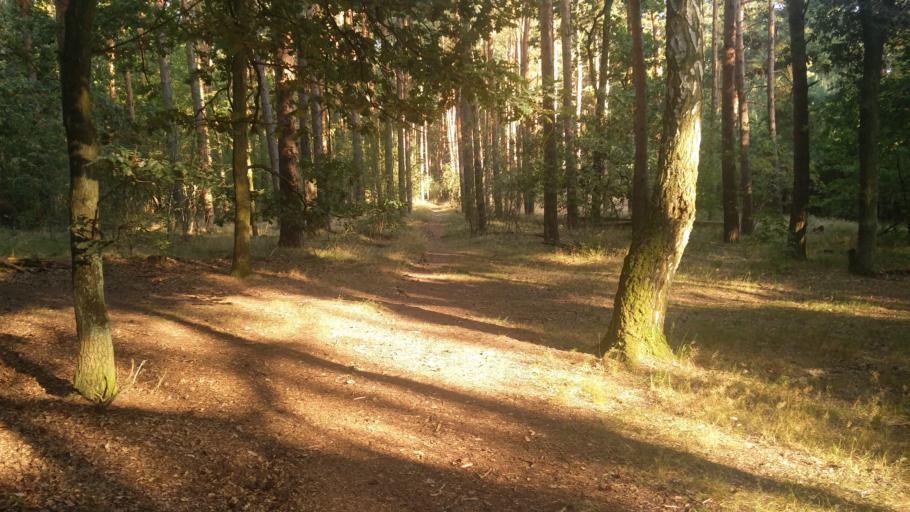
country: DE
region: Berlin
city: Friedrichshagen
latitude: 52.4451
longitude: 13.6107
